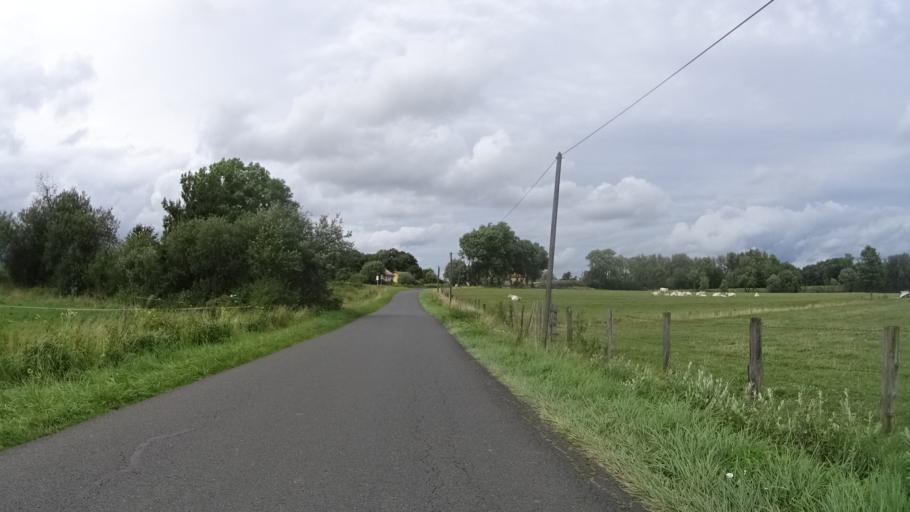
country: FR
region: Lorraine
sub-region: Departement de la Moselle
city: Sarrebourg
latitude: 48.7056
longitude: 7.0700
